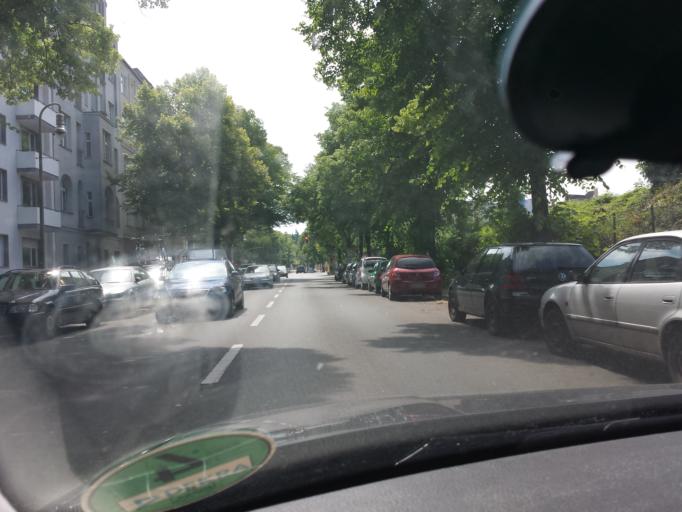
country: DE
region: Berlin
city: Bezirk Kreuzberg
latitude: 52.4936
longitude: 13.3795
